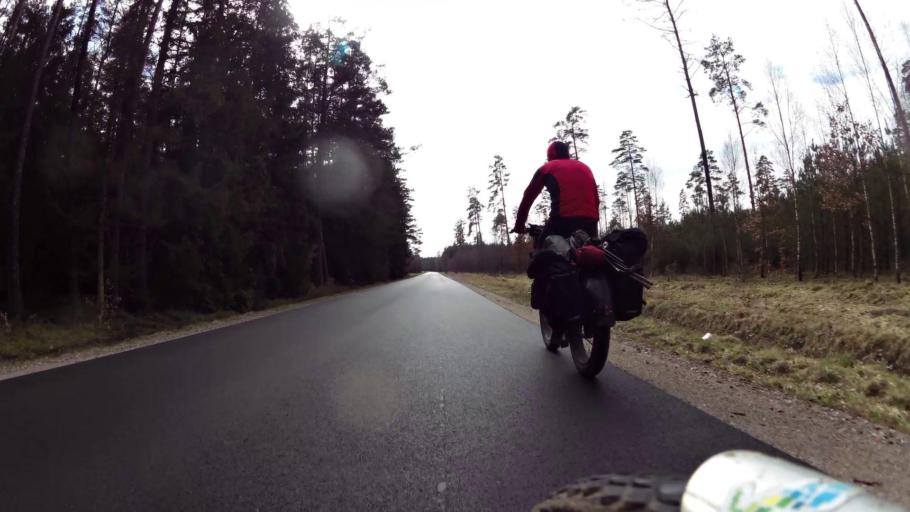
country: PL
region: Pomeranian Voivodeship
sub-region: Powiat bytowski
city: Kolczyglowy
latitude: 54.2014
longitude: 17.2351
